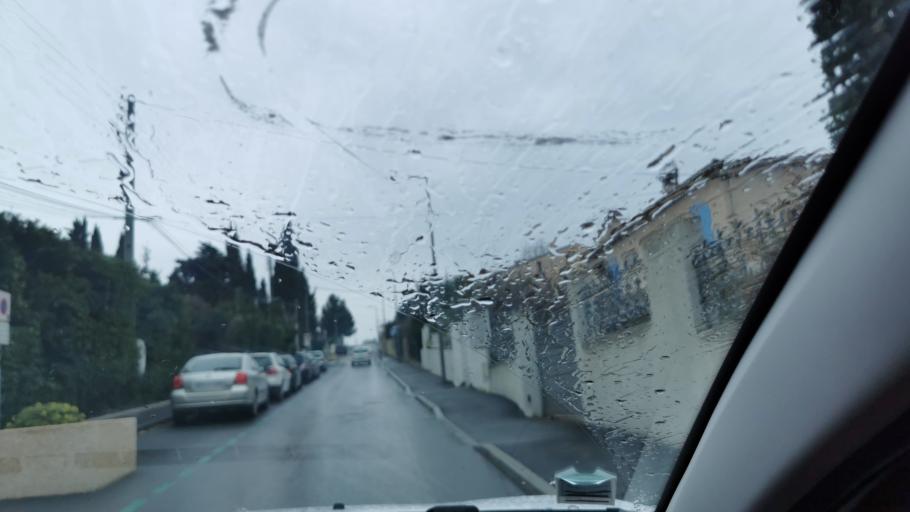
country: FR
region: Provence-Alpes-Cote d'Azur
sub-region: Departement des Bouches-du-Rhone
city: Lambesc
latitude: 43.6529
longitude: 5.2653
